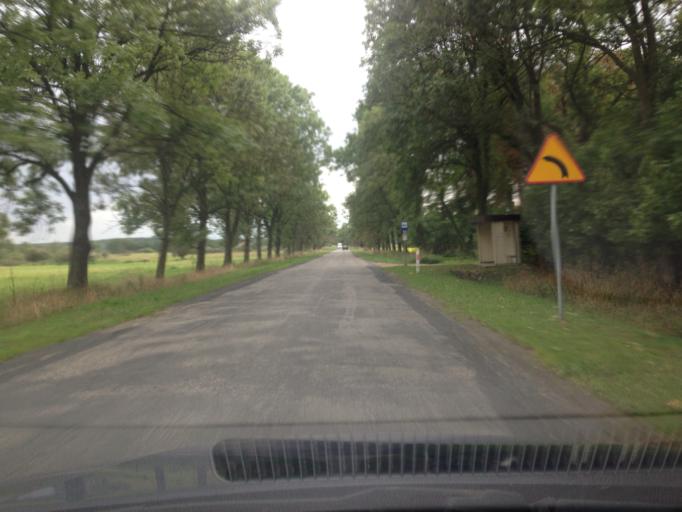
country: PL
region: Kujawsko-Pomorskie
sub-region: Powiat lipnowski
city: Lipno
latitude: 52.7881
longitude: 19.2087
